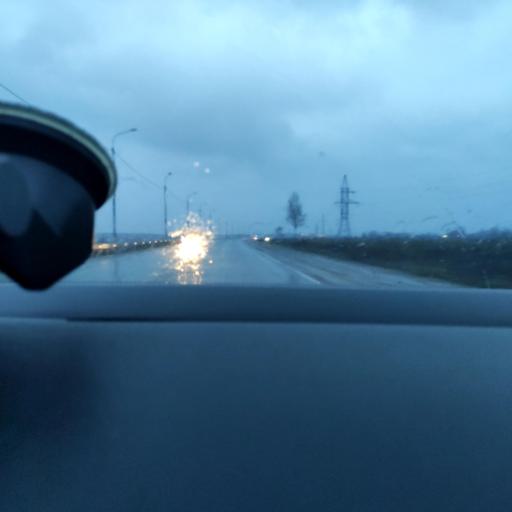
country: RU
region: Moskovskaya
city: Yegor'yevsk
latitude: 55.3958
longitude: 39.0670
